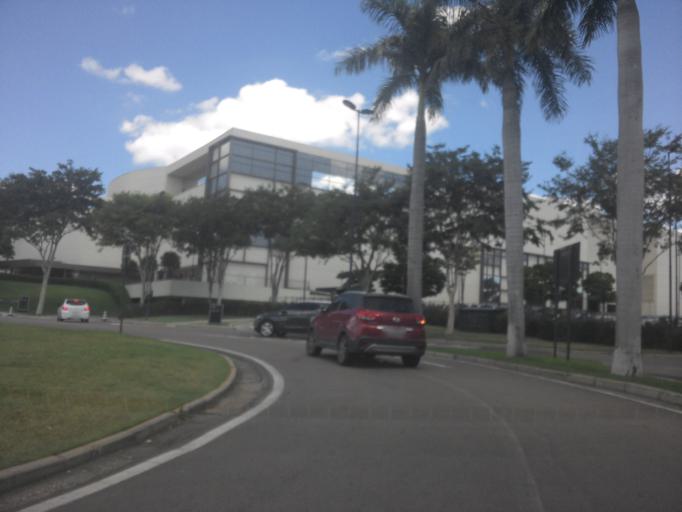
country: BR
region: Sao Paulo
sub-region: Campinas
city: Campinas
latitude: -22.8912
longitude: -47.0252
